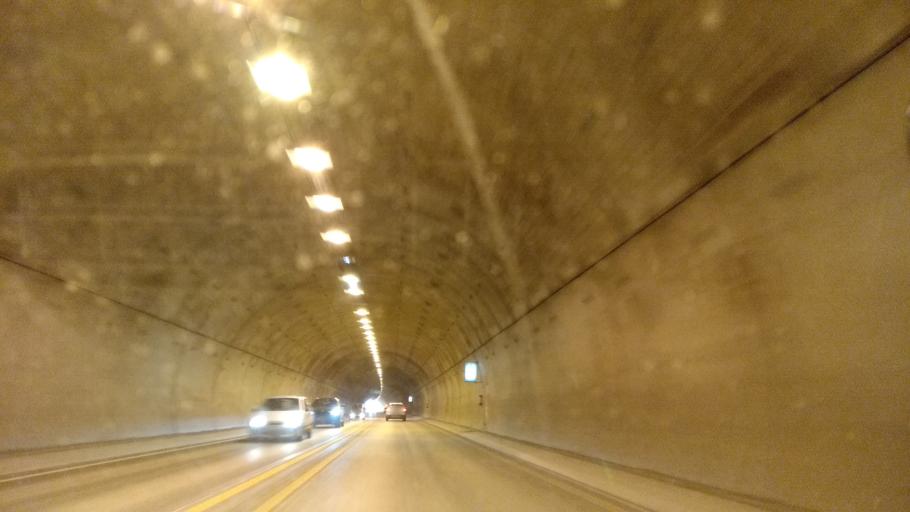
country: NO
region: Rogaland
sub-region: Klepp
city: Kleppe
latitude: 58.7773
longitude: 5.6219
